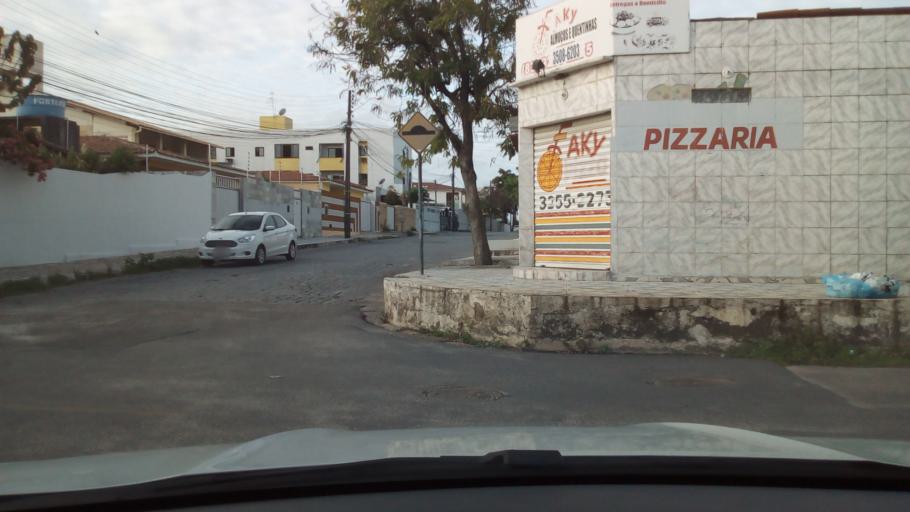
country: BR
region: Paraiba
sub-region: Joao Pessoa
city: Joao Pessoa
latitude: -7.1532
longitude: -34.8308
